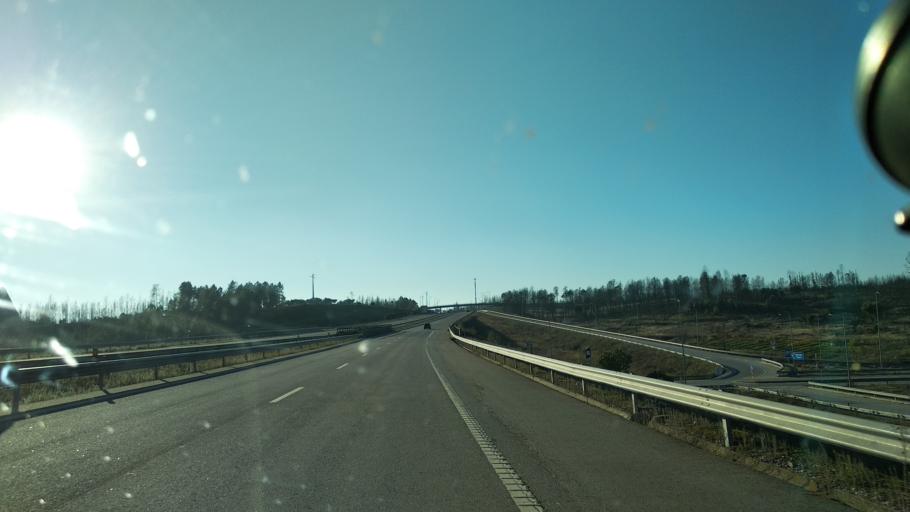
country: PT
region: Santarem
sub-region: Macao
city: Macao
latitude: 39.5308
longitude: -7.9459
